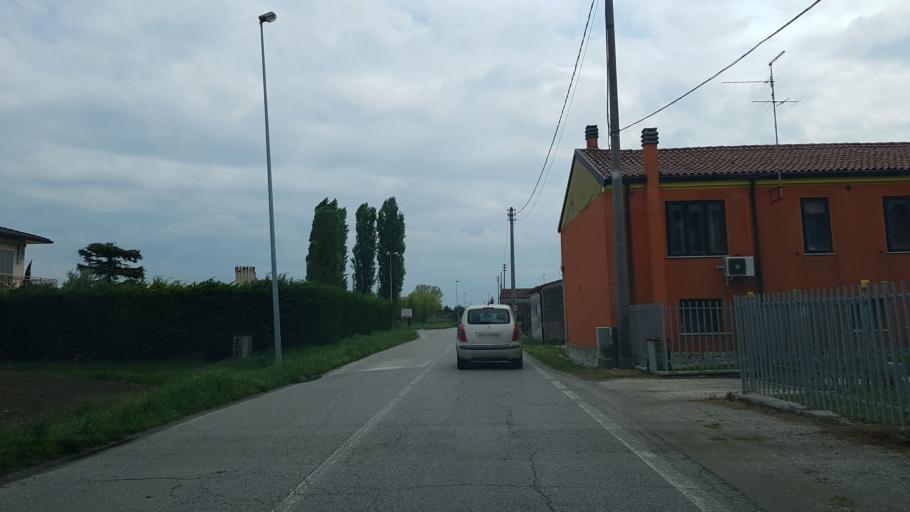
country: IT
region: Veneto
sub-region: Provincia di Verona
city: Maccacari
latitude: 45.1516
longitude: 11.1343
